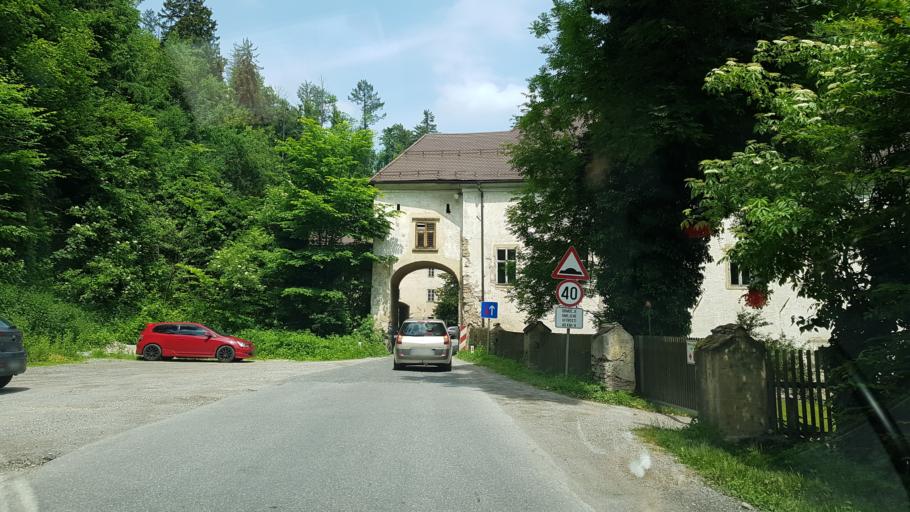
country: SI
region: Vrhnika
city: Verd
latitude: 45.9457
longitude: 14.3329
